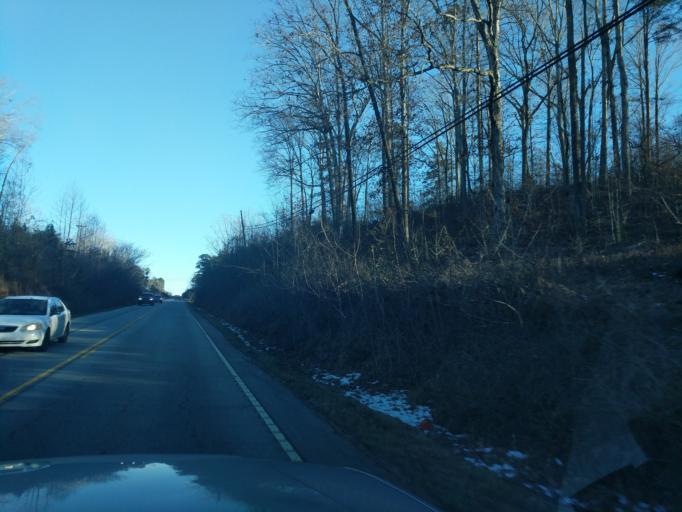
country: US
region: South Carolina
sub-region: Oconee County
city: Westminster
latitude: 34.6867
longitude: -83.1384
